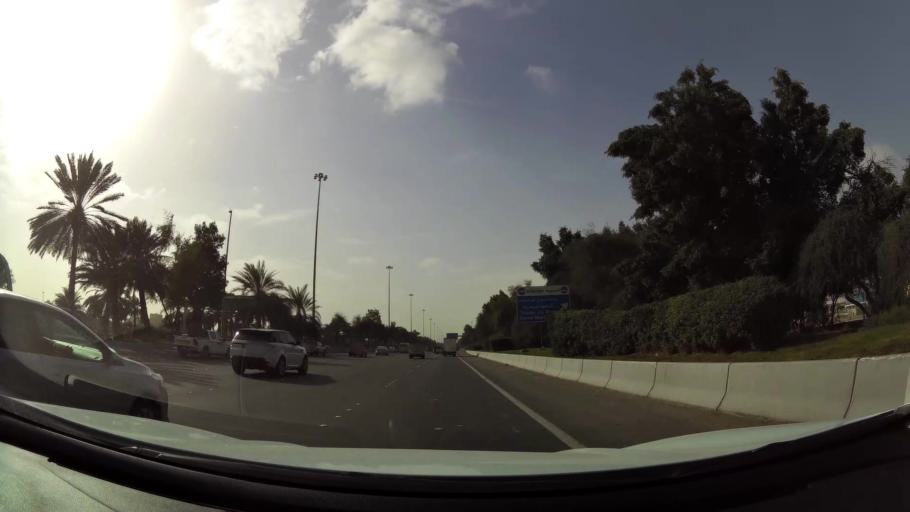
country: AE
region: Abu Dhabi
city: Abu Dhabi
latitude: 24.4109
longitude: 54.5126
